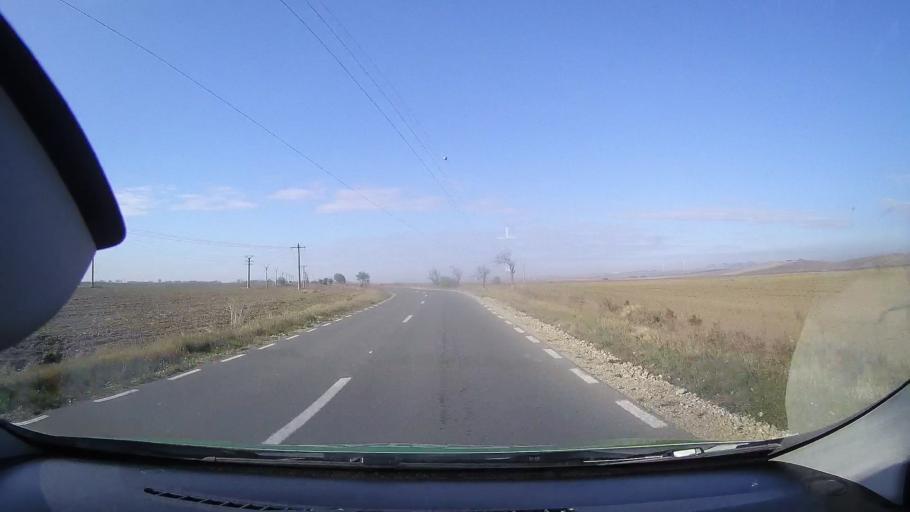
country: RO
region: Tulcea
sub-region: Comuna Murighiol
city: Murighiol
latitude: 45.0284
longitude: 29.1495
